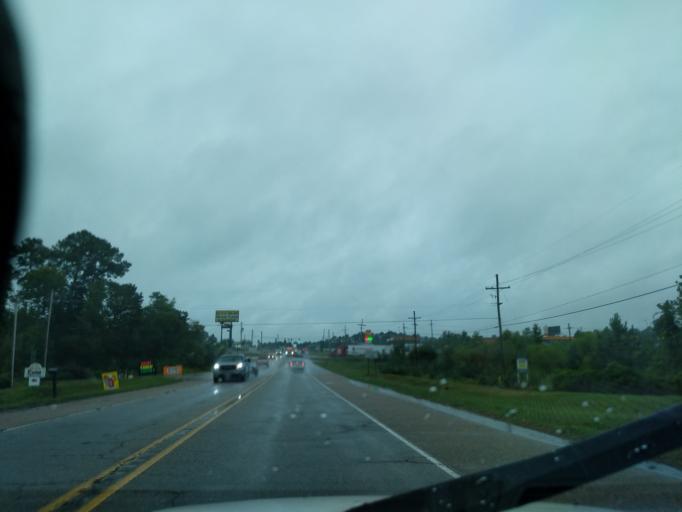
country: US
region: Louisiana
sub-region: Webster Parish
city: Minden
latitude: 32.5845
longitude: -93.2479
